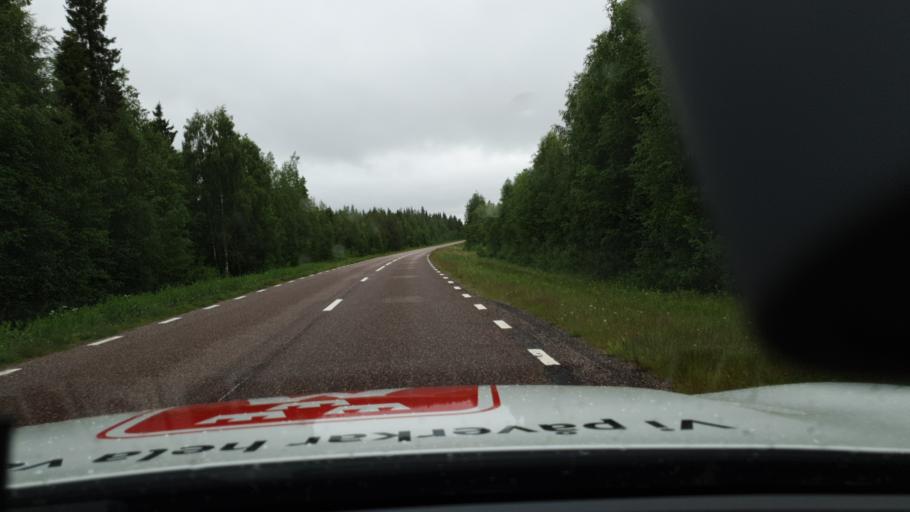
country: FI
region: Lapland
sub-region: Torniolaakso
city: Pello
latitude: 66.9176
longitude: 23.8573
